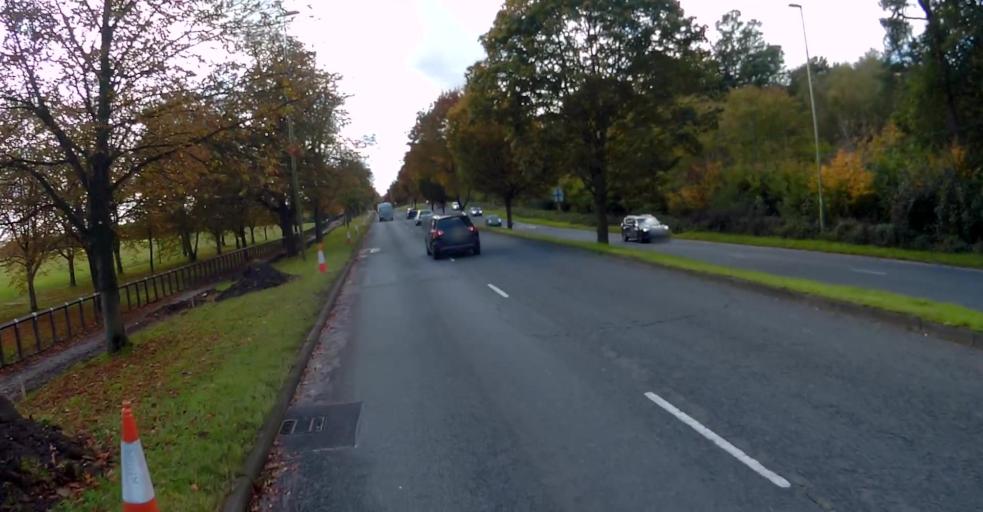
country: GB
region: England
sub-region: Hampshire
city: Aldershot
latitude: 51.2704
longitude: -0.7593
